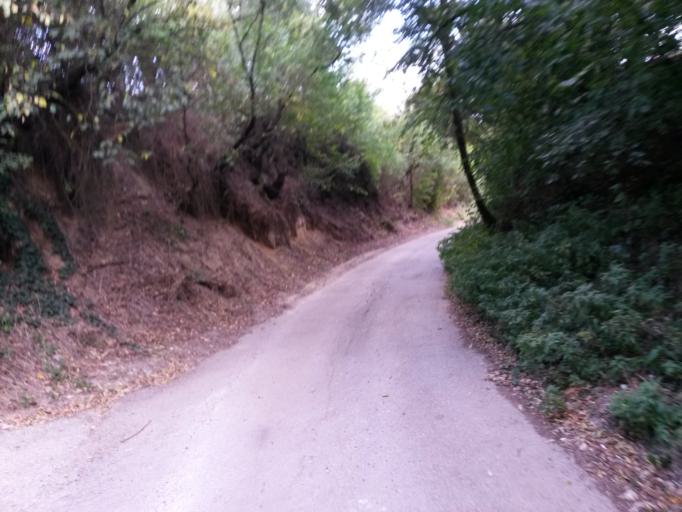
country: HU
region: Pest
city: Budaors
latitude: 47.4715
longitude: 18.9600
